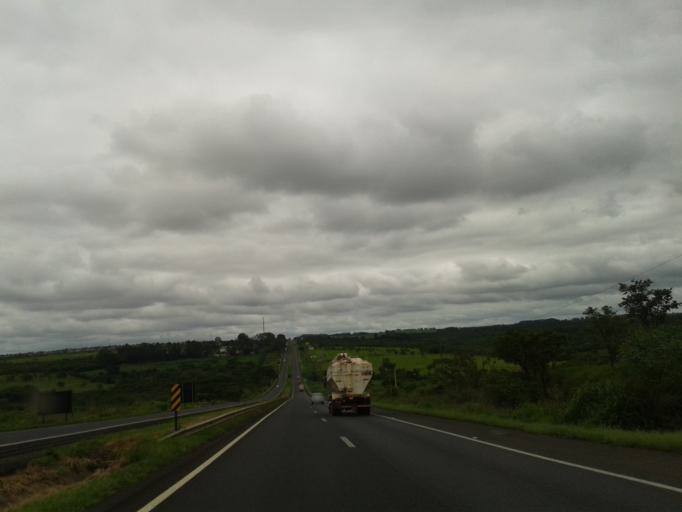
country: BR
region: Minas Gerais
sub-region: Uberlandia
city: Uberlandia
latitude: -18.9945
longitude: -48.2107
